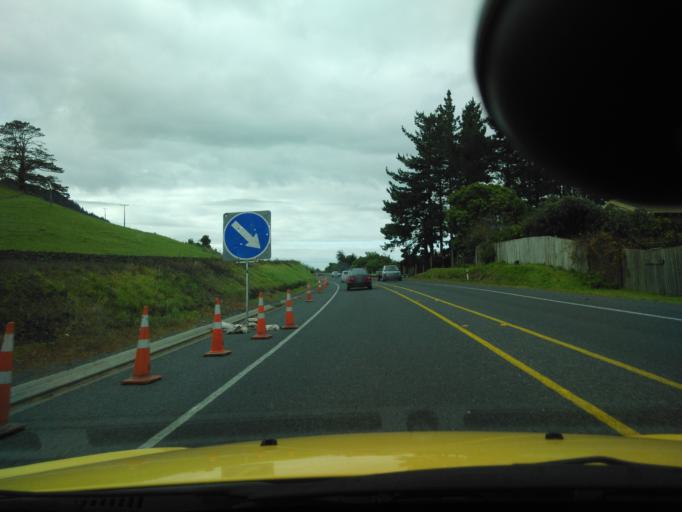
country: NZ
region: Waikato
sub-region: Waikato District
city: Ngaruawahia
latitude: -37.5990
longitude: 175.1643
